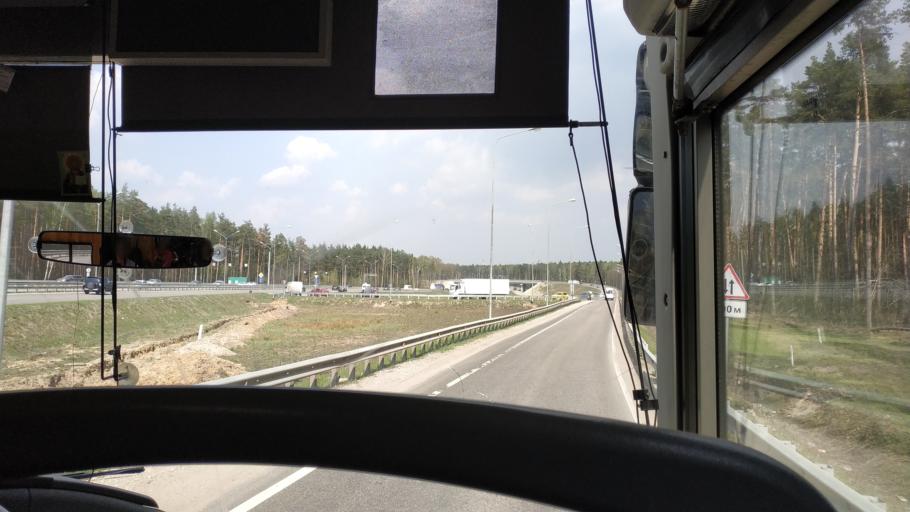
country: RU
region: Moskovskaya
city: Lytkarino
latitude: 55.6170
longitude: 37.9227
